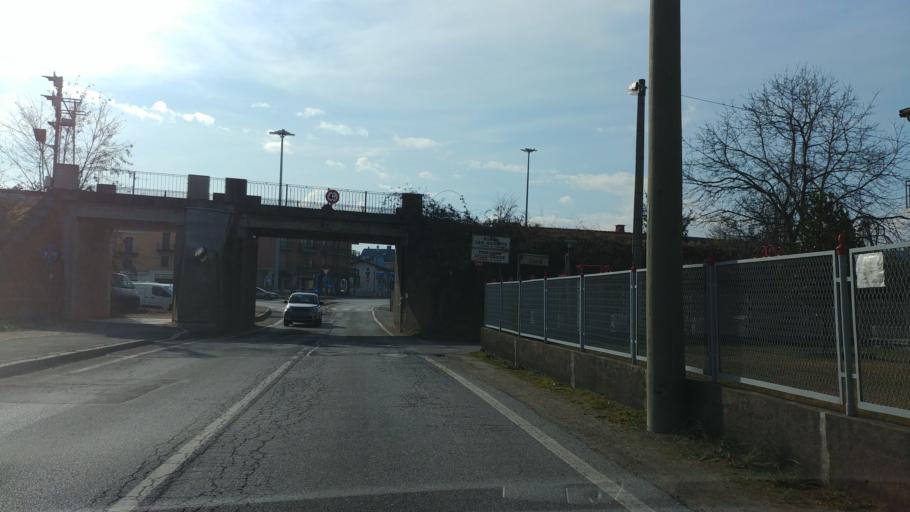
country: IT
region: Piedmont
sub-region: Provincia di Cuneo
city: Cuneo
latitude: 44.3924
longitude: 7.5636
